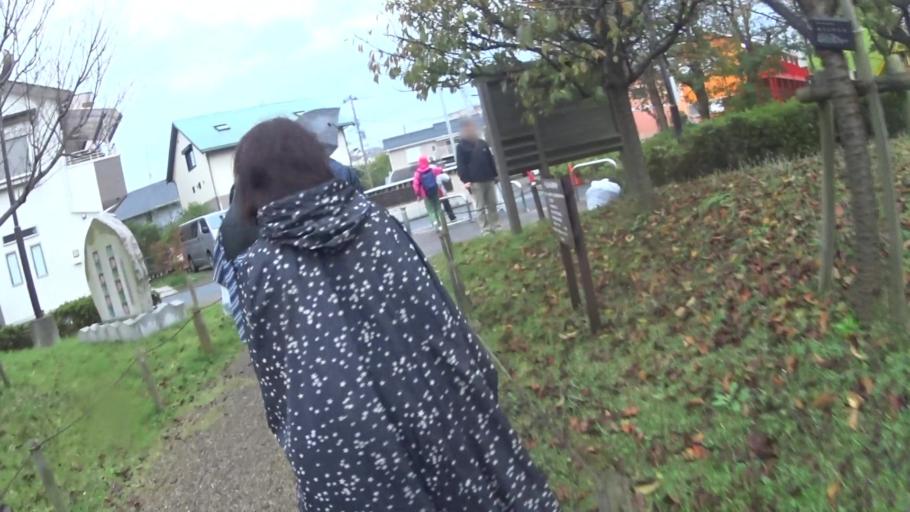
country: JP
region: Kanagawa
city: Hadano
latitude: 35.3672
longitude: 139.2230
